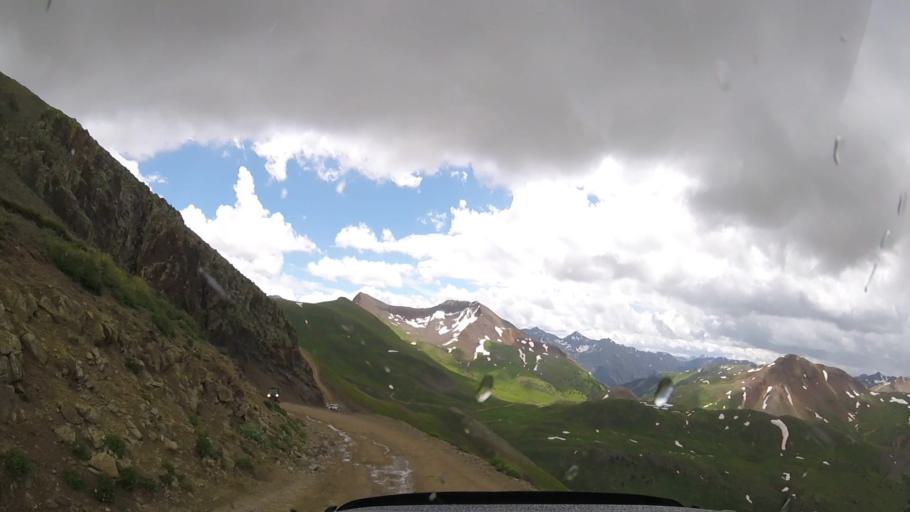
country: US
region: Colorado
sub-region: Ouray County
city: Ouray
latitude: 37.9665
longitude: -107.5858
